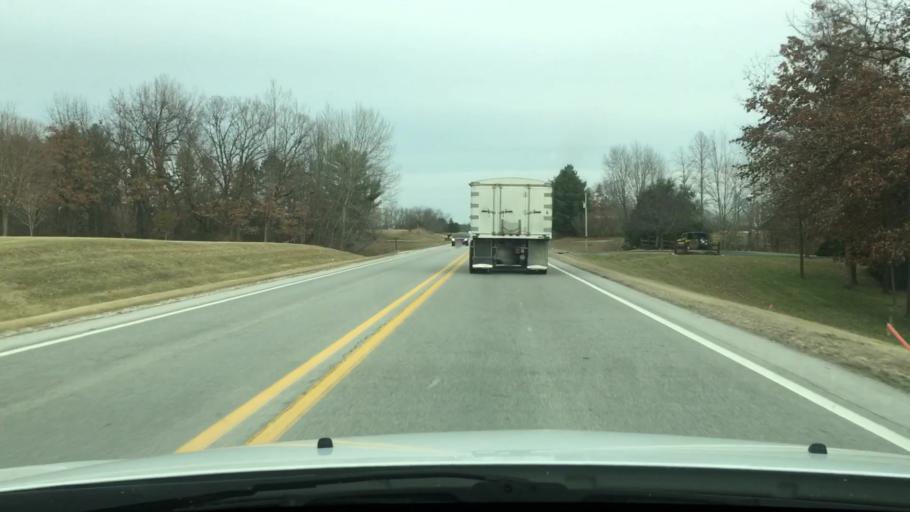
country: US
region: Illinois
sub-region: Pike County
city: Pittsfield
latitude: 39.6556
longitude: -90.7808
